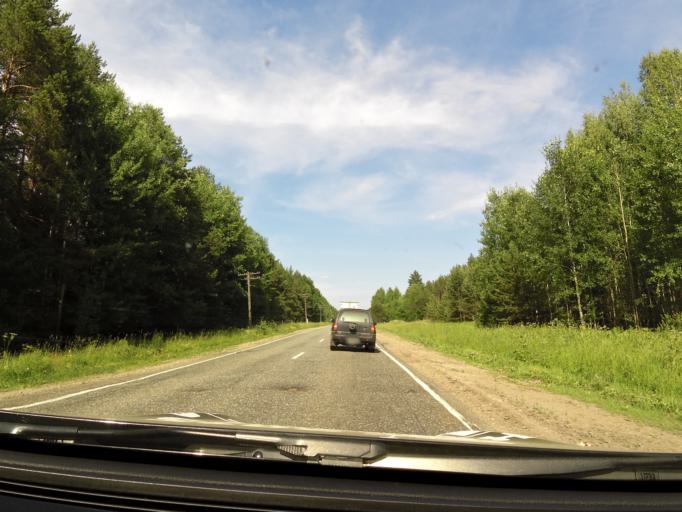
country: RU
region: Kirov
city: Belaya Kholunitsa
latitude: 58.7910
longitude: 50.5164
